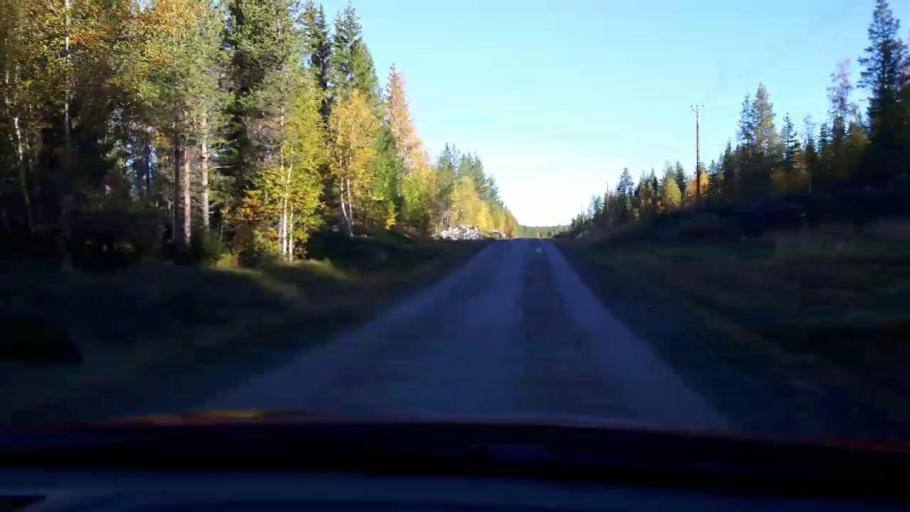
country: SE
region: Jaemtland
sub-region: Stroemsunds Kommun
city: Stroemsund
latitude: 64.3747
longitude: 15.1514
